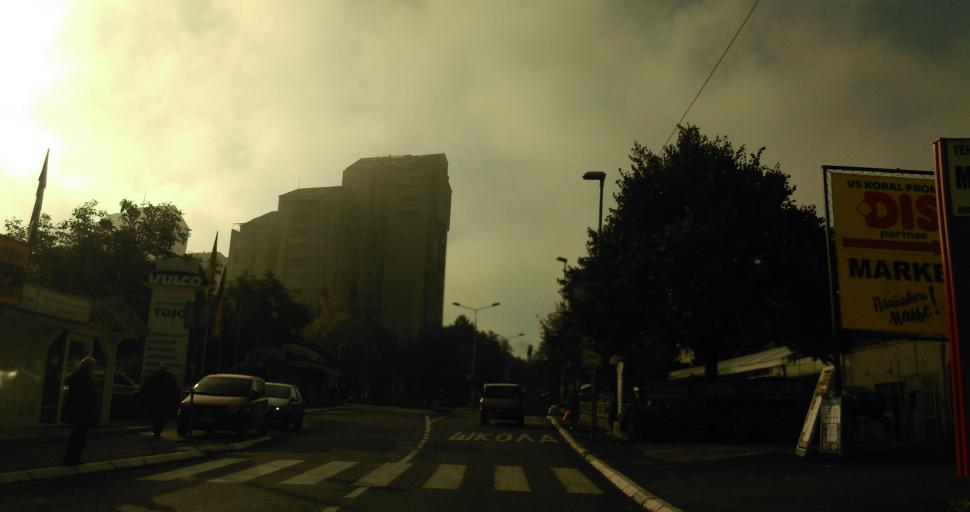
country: RS
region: Central Serbia
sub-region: Belgrade
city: Rakovica
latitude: 44.7314
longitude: 20.4209
